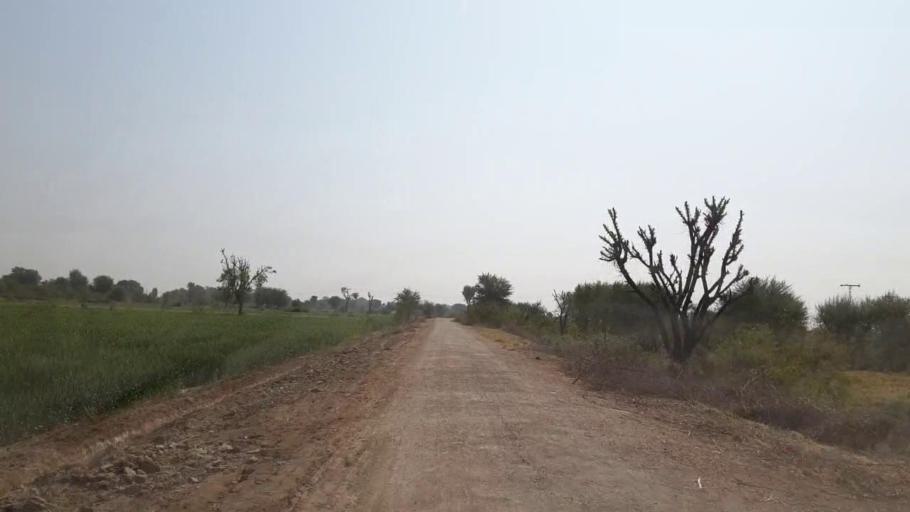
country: PK
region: Sindh
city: Mirpur Khas
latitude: 25.6296
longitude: 69.1437
